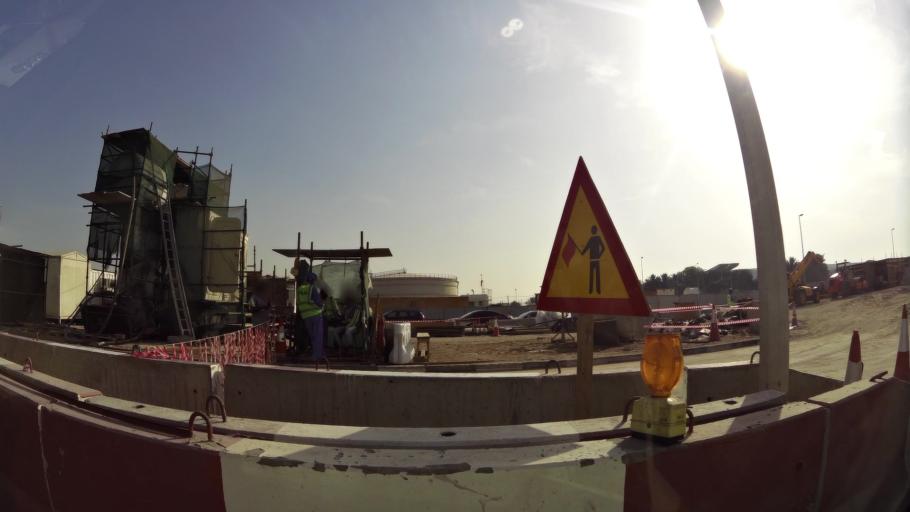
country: AE
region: Ash Shariqah
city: Sharjah
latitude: 25.2327
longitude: 55.3864
